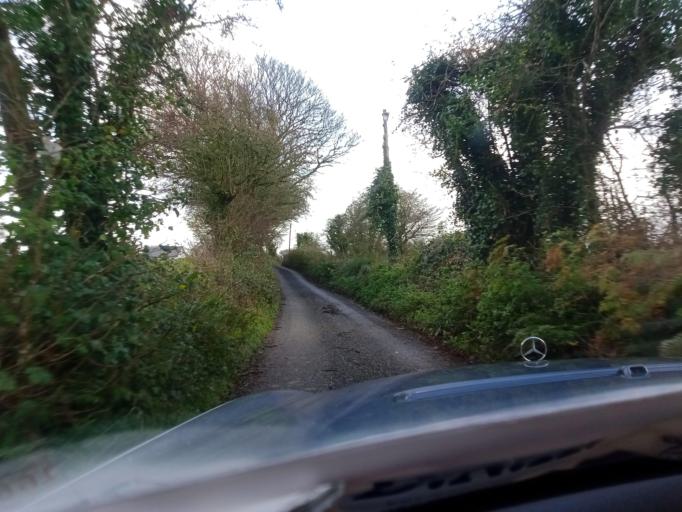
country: IE
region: Leinster
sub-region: Kilkenny
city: Mooncoin
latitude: 52.2851
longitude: -7.2667
